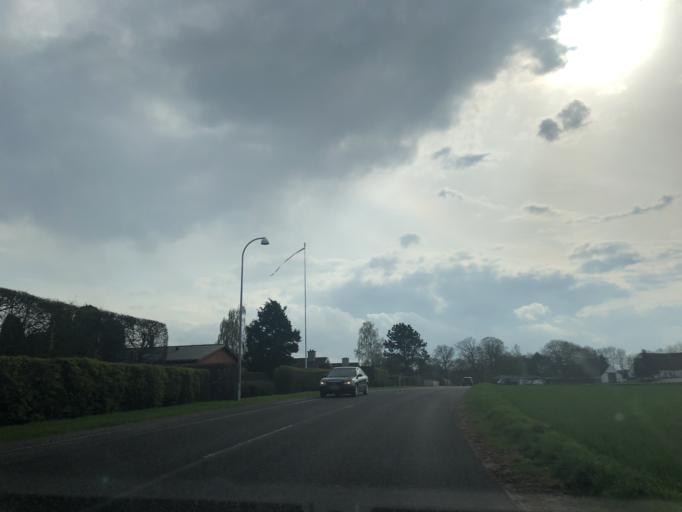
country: DK
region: Zealand
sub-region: Roskilde Kommune
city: Gundsomagle
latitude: 55.6980
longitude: 12.1381
